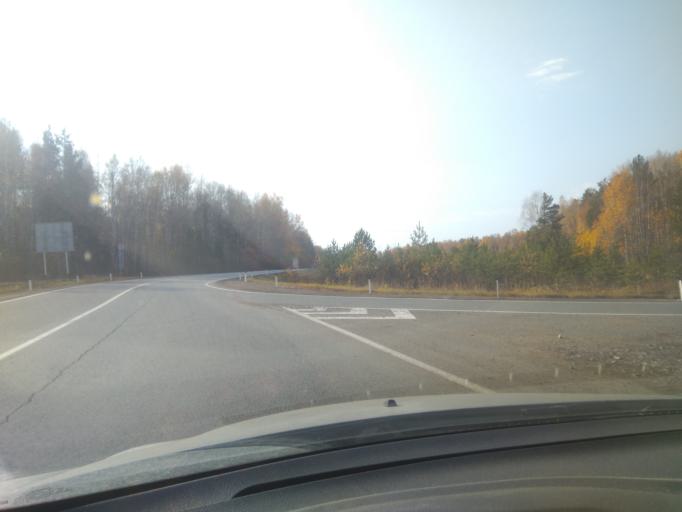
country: RU
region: Sverdlovsk
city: Atig
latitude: 56.7336
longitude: 59.4315
